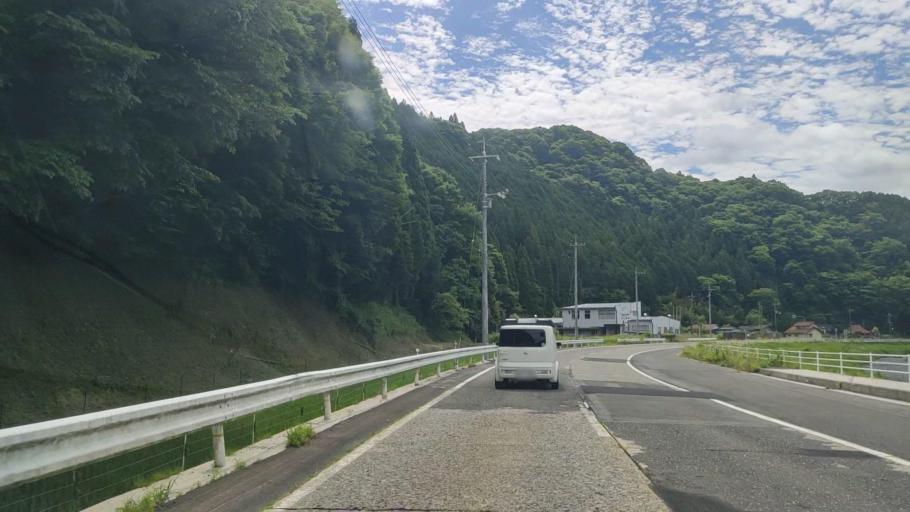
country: JP
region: Okayama
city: Niimi
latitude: 35.1715
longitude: 133.5780
